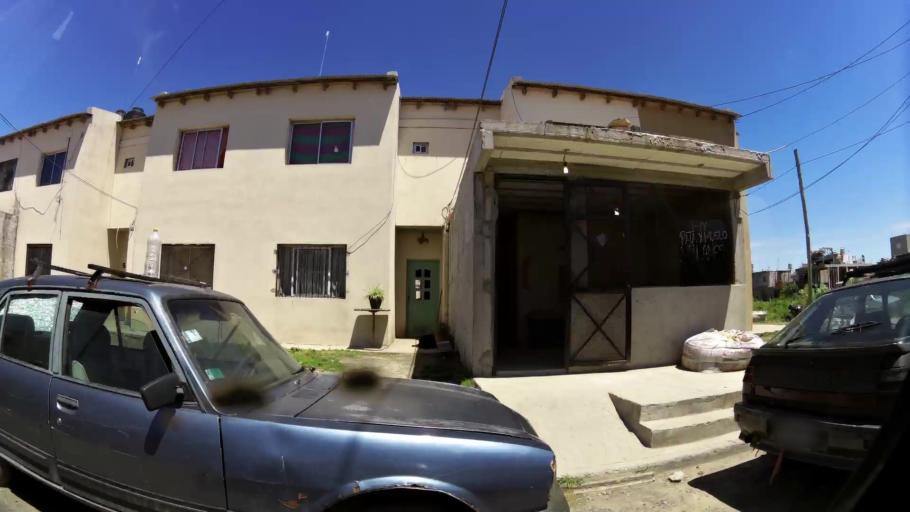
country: AR
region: Buenos Aires
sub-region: Partido de Quilmes
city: Quilmes
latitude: -34.7144
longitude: -58.3151
